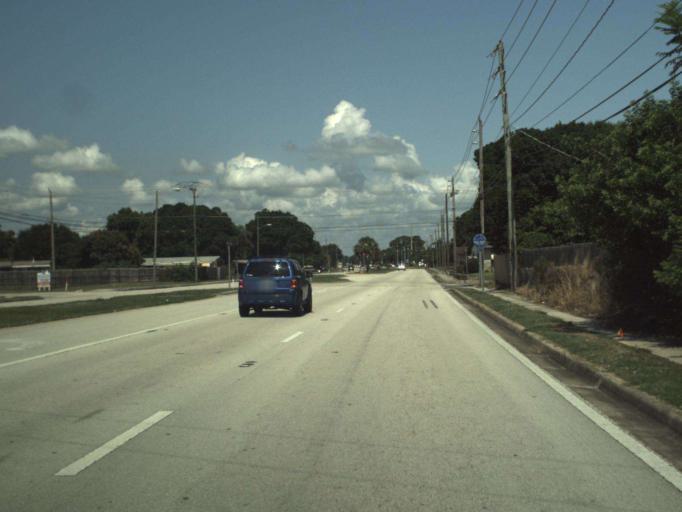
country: US
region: Florida
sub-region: Brevard County
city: June Park
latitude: 28.1286
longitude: -80.6662
